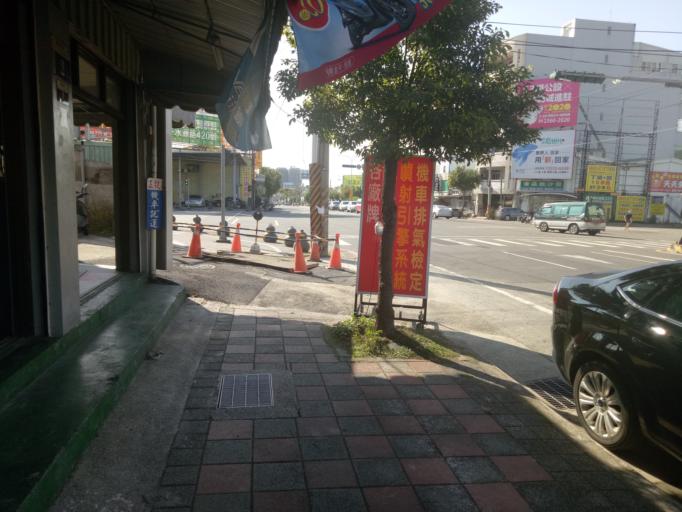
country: TW
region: Taiwan
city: Fengyuan
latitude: 24.2607
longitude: 120.7363
